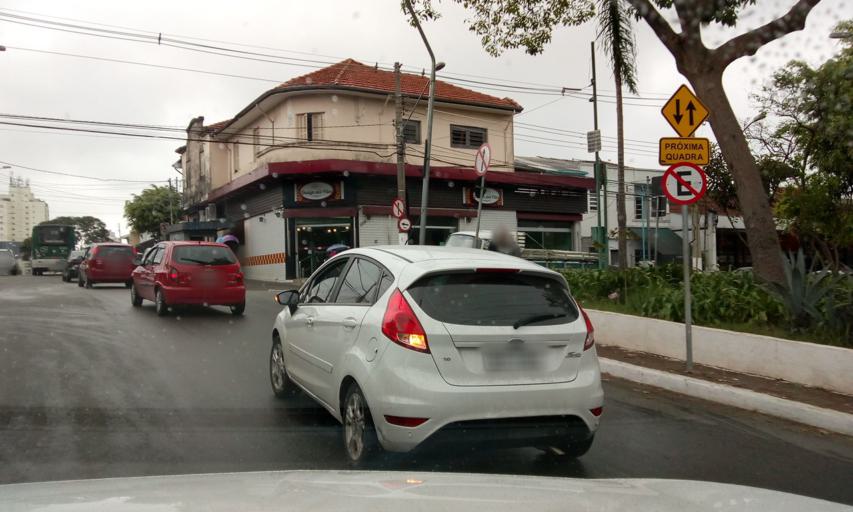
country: BR
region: Sao Paulo
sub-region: Sao Paulo
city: Sao Paulo
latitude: -23.5819
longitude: -46.6265
